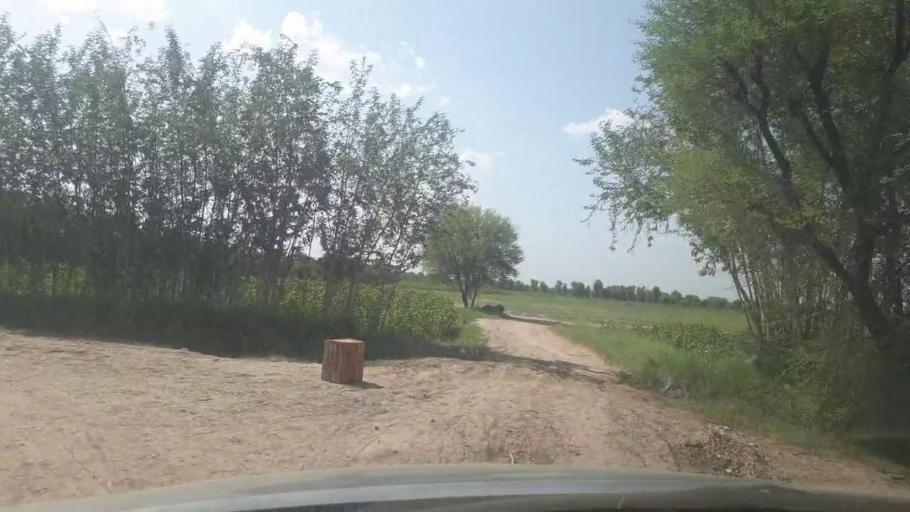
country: PK
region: Sindh
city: Khairpur
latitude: 27.5525
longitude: 68.8091
